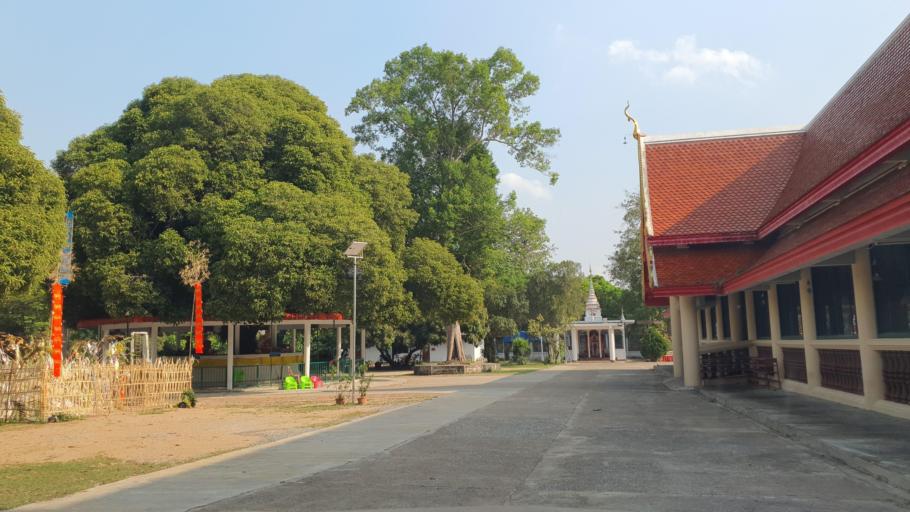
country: TH
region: Chiang Mai
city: San Pa Tong
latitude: 18.6512
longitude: 98.8484
